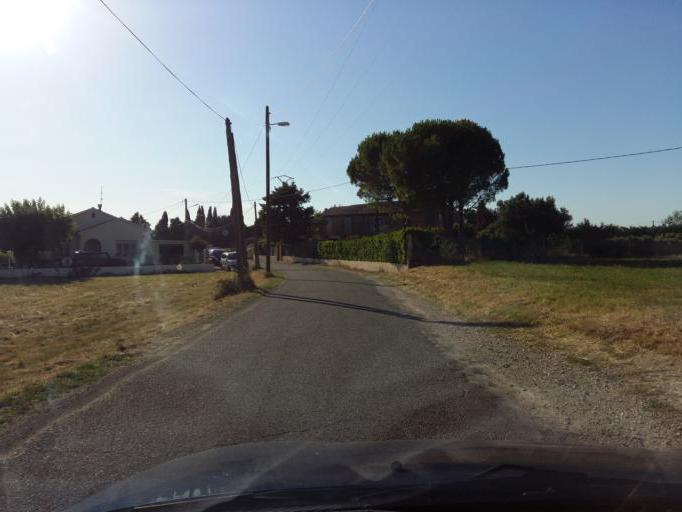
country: FR
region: Provence-Alpes-Cote d'Azur
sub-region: Departement du Vaucluse
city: Camaret-sur-Aigues
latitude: 44.1669
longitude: 4.8882
